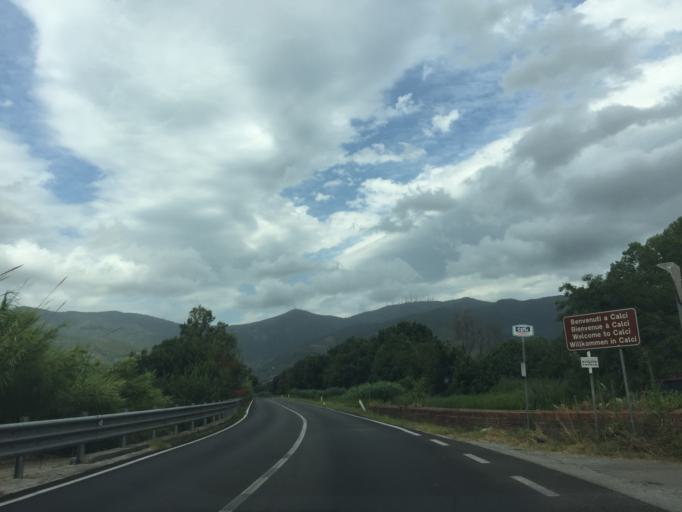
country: IT
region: Tuscany
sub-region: Province of Pisa
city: Gabella
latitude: 43.7093
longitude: 10.5054
